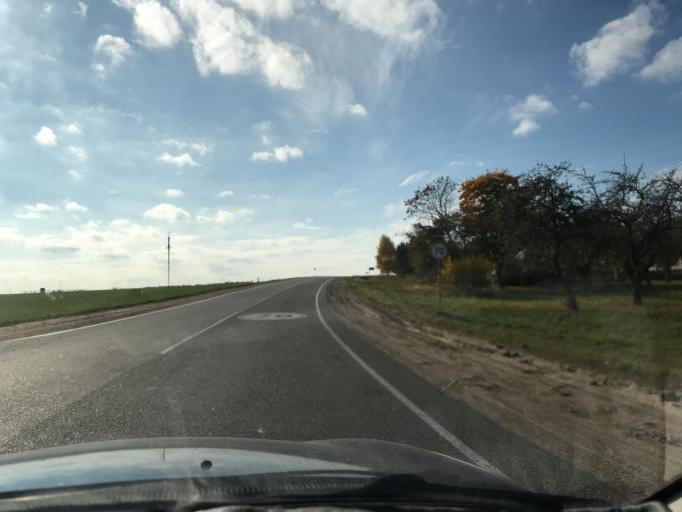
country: BY
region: Grodnenskaya
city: Voranava
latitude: 54.1459
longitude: 25.3269
